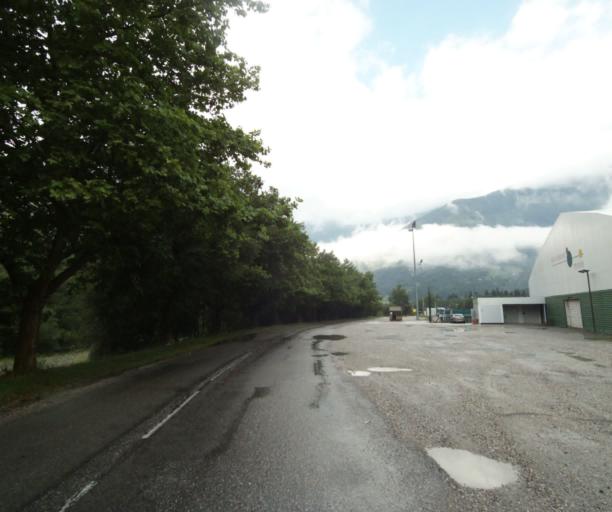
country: FR
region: Rhone-Alpes
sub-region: Departement de la Haute-Savoie
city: Thones
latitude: 45.8888
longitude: 6.3089
